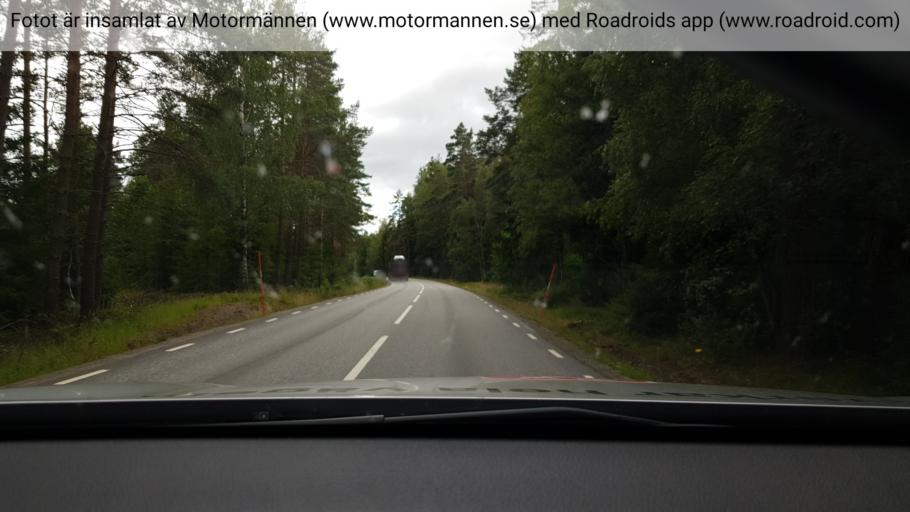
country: SE
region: Stockholm
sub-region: Haninge Kommun
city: Haninge
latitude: 59.1589
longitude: 18.1809
